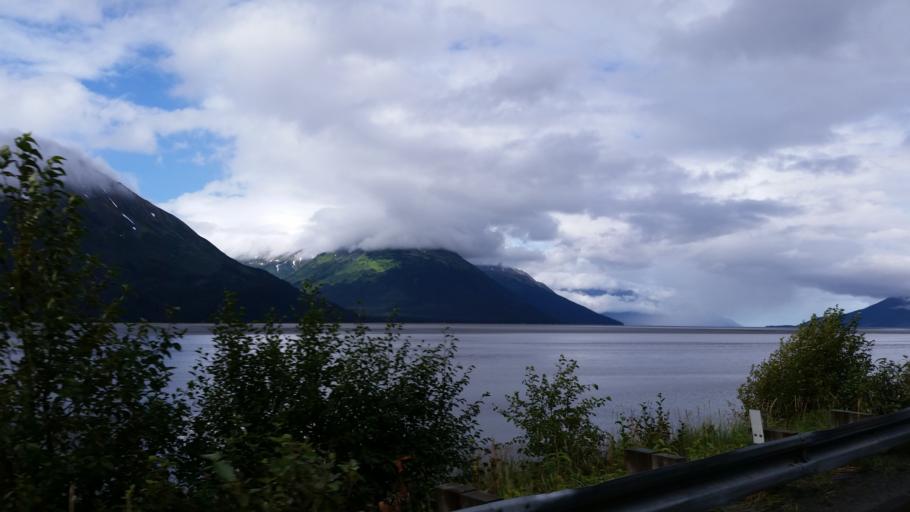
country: US
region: Alaska
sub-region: Anchorage Municipality
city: Girdwood
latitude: 60.8894
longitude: -149.0562
